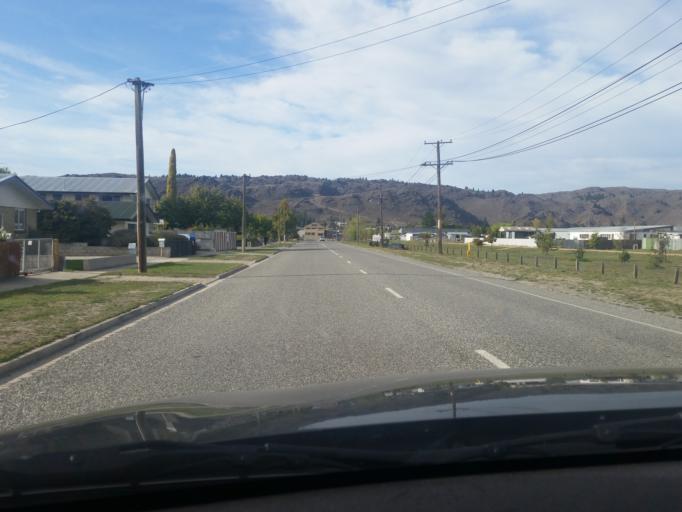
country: NZ
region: Otago
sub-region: Queenstown-Lakes District
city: Wanaka
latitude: -45.2423
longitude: 169.3918
